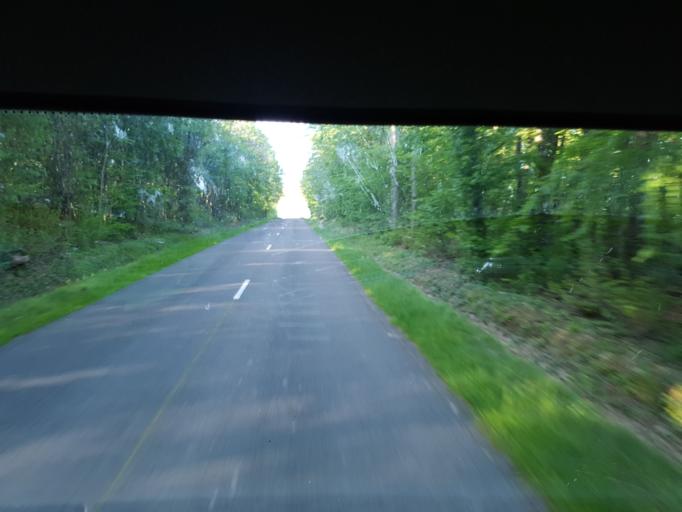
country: FR
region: Champagne-Ardenne
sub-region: Departement de l'Aube
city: Marigny-le-Chatel
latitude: 48.3771
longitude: 3.6433
